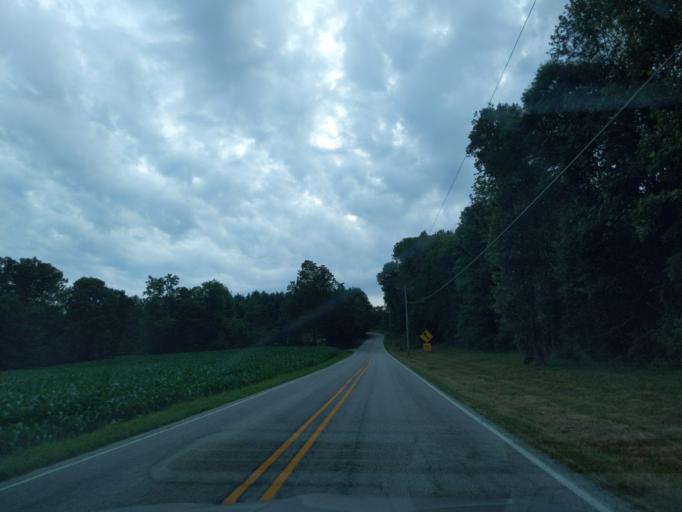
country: US
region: Indiana
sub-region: Ripley County
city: Osgood
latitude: 39.1950
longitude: -85.2563
